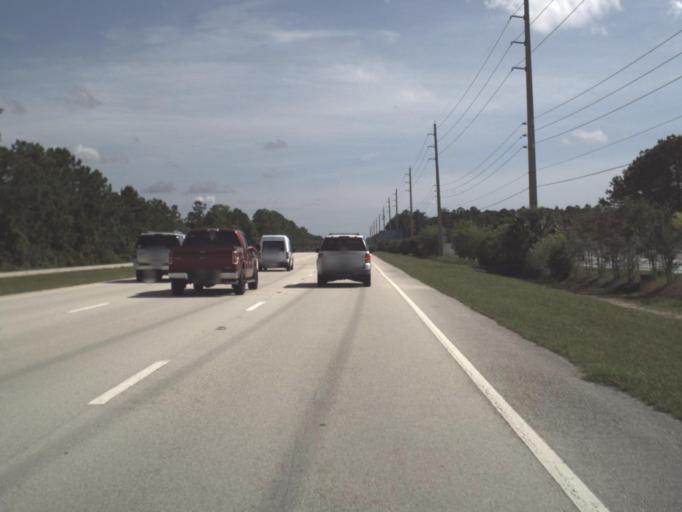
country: US
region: Florida
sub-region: Clay County
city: Orange Park
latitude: 30.2115
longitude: -81.7047
